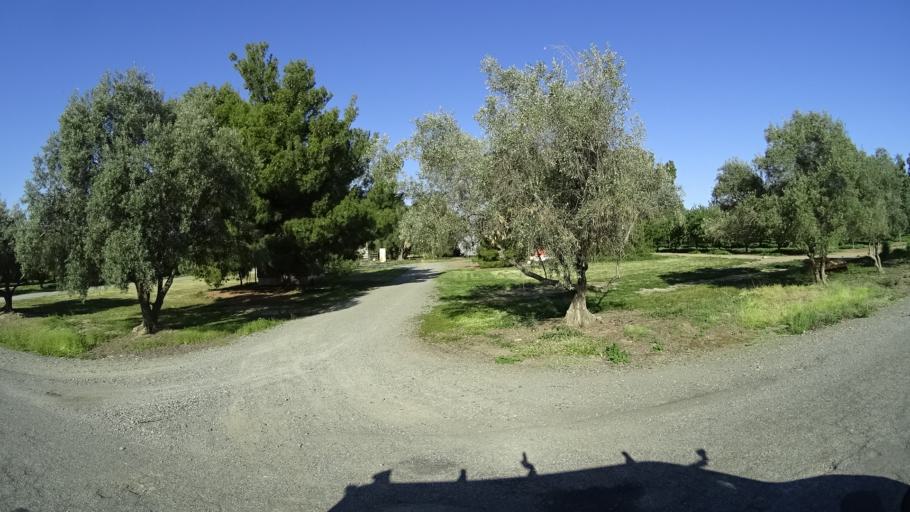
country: US
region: California
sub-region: Glenn County
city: Orland
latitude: 39.6826
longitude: -122.1220
